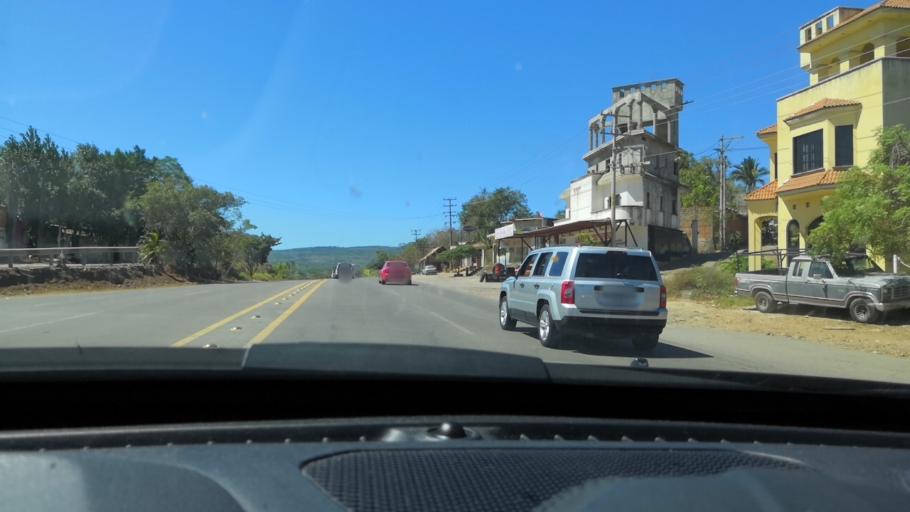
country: MX
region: Nayarit
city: Las Varas
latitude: 21.1762
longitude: -105.1422
